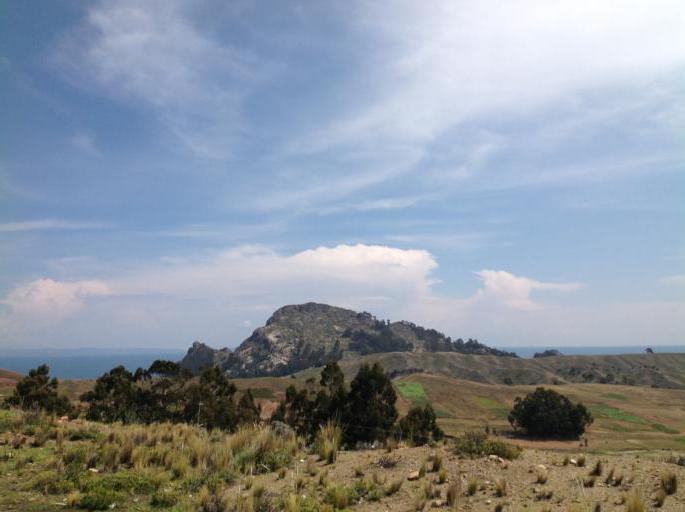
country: BO
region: La Paz
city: Yumani
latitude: -15.8458
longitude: -68.9906
